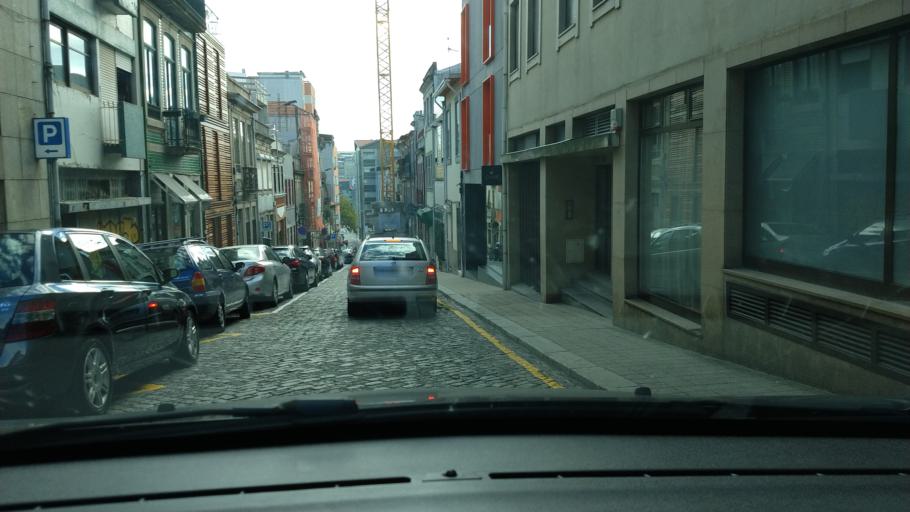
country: PT
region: Porto
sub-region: Porto
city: Porto
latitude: 41.1527
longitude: -8.6115
